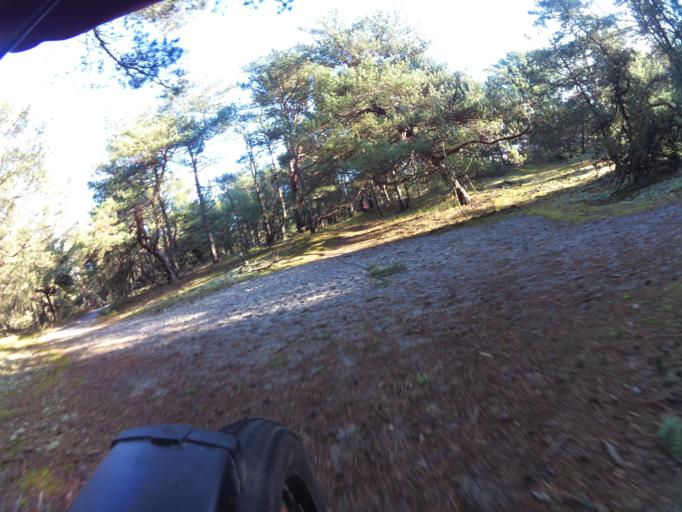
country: PL
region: Pomeranian Voivodeship
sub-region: Powiat pucki
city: Hel
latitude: 54.6057
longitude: 18.8227
